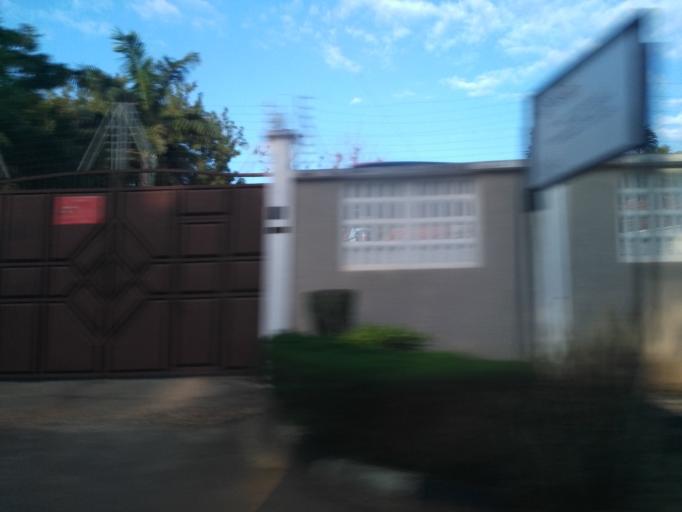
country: TZ
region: Dar es Salaam
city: Magomeni
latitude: -6.7831
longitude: 39.2720
